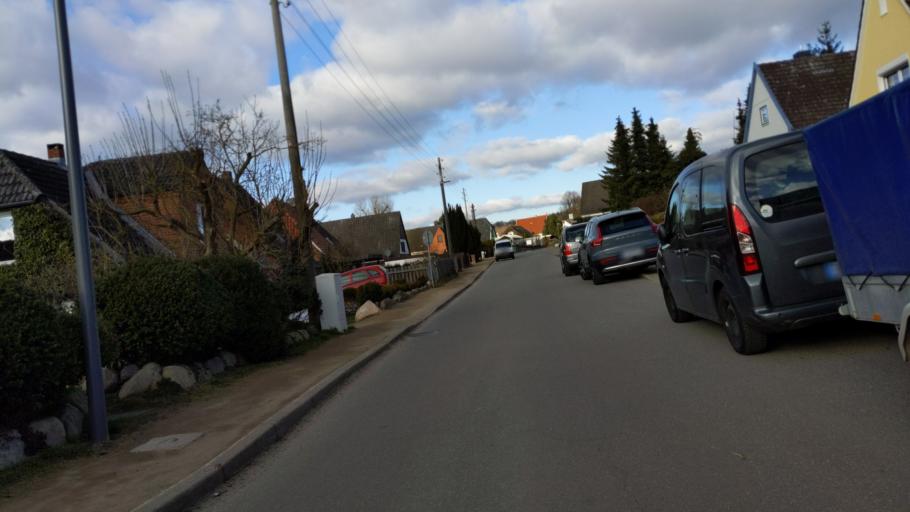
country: DE
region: Schleswig-Holstein
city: Susel
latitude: 54.0805
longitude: 10.7138
